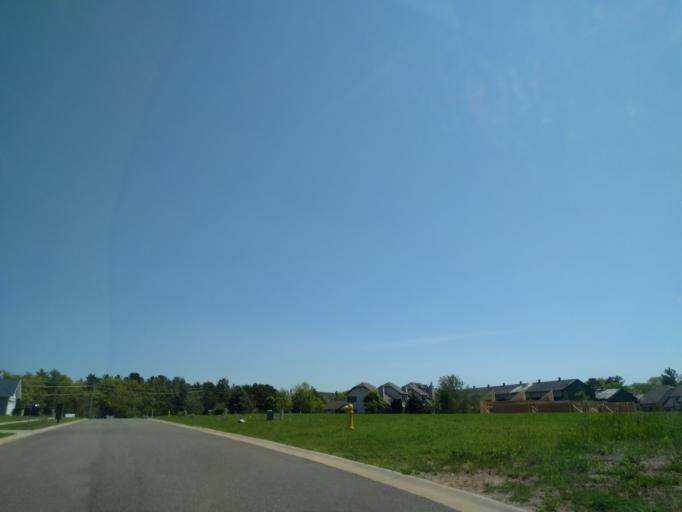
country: US
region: Michigan
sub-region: Marquette County
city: Marquette
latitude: 46.5561
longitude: -87.3848
